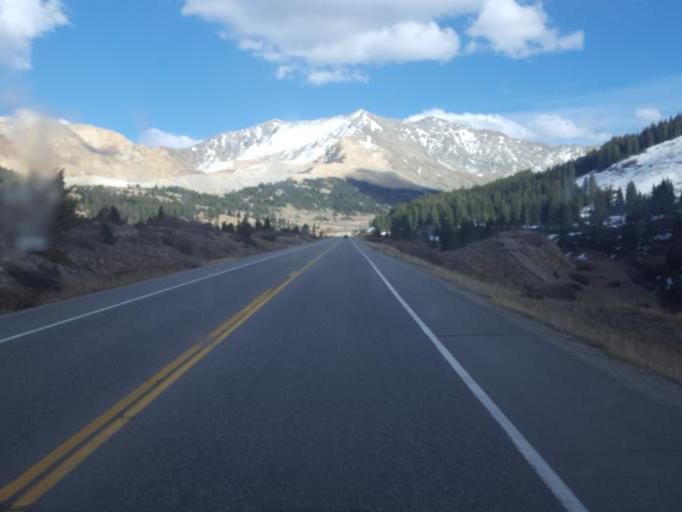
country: US
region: Colorado
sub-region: Lake County
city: Leadville
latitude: 39.3603
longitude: -106.2028
